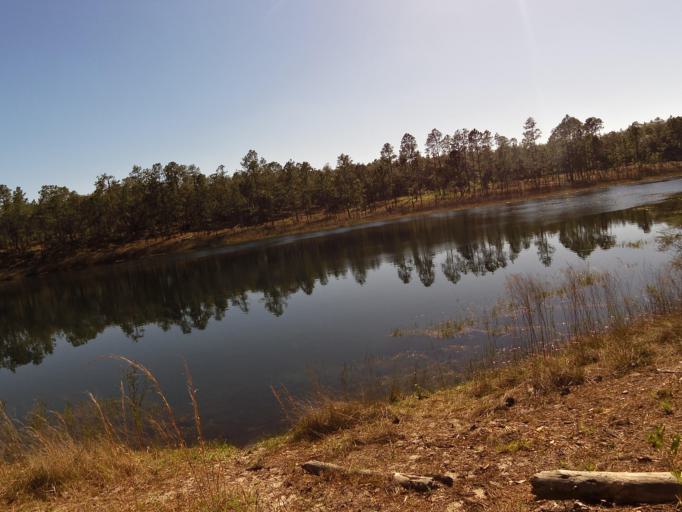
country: US
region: Florida
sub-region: Clay County
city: Keystone Heights
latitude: 29.8186
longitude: -82.0076
